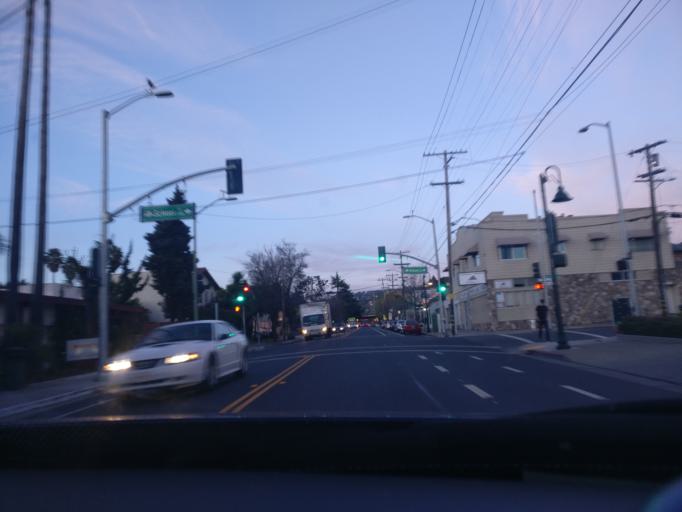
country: US
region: California
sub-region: Alameda County
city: Piedmont
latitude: 37.7956
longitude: -122.2180
